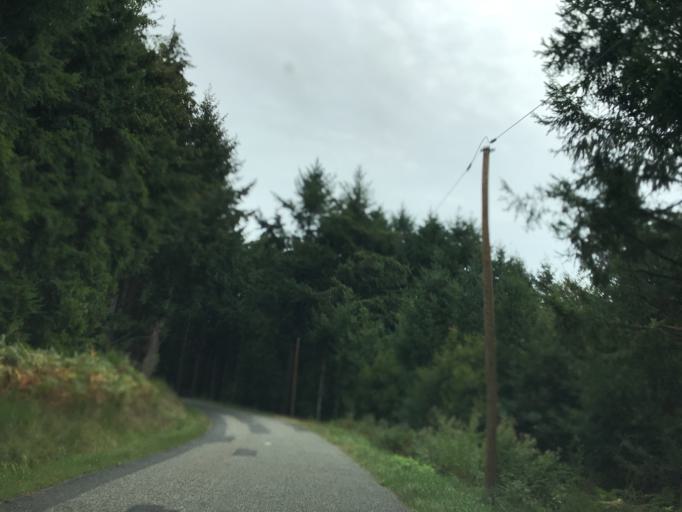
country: FR
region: Rhone-Alpes
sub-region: Departement de la Loire
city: Sail-sous-Couzan
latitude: 45.6881
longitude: 3.9148
